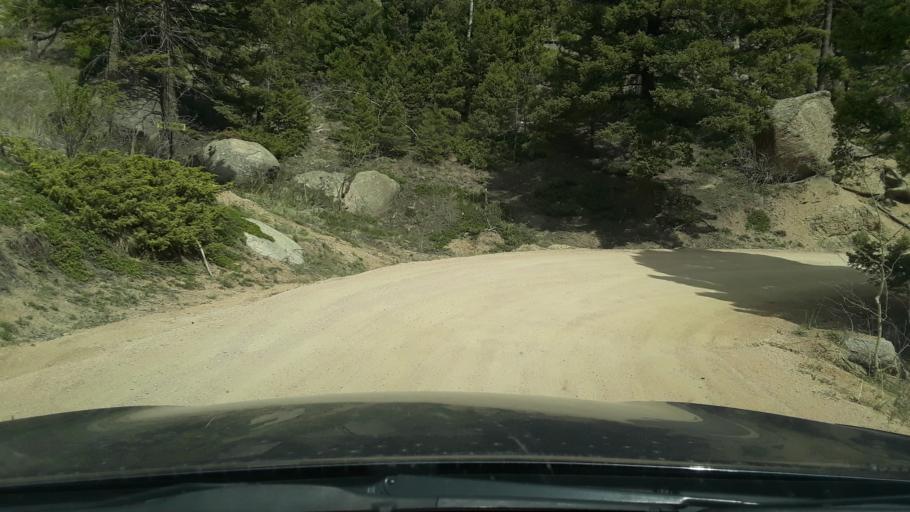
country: US
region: Colorado
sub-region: El Paso County
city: Palmer Lake
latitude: 39.0698
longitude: -104.9405
